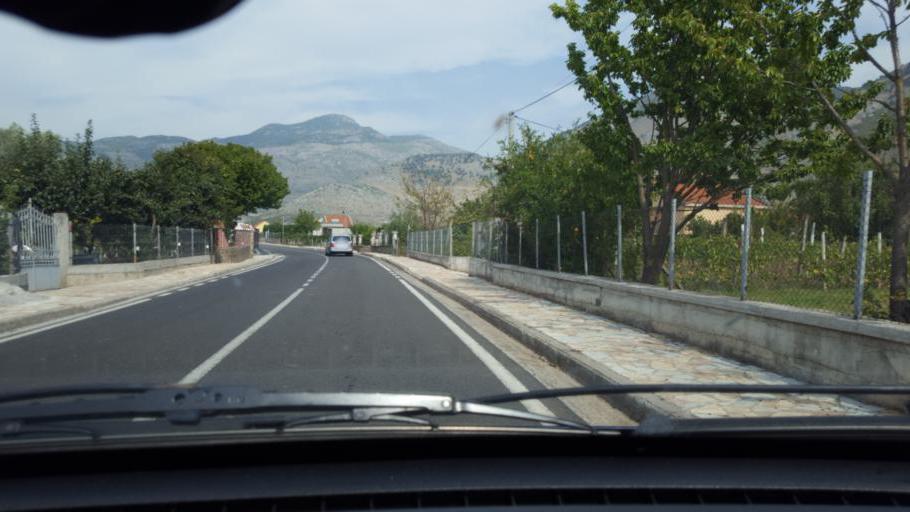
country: AL
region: Shkoder
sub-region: Rrethi i Malesia e Madhe
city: Hot
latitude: 42.3426
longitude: 19.4387
